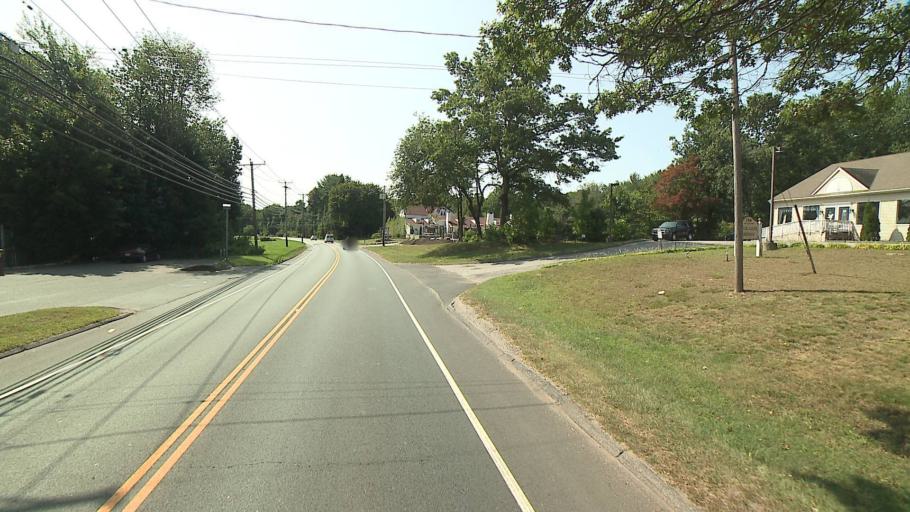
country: US
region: Connecticut
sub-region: Fairfield County
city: Newtown
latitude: 41.3839
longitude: -73.2849
